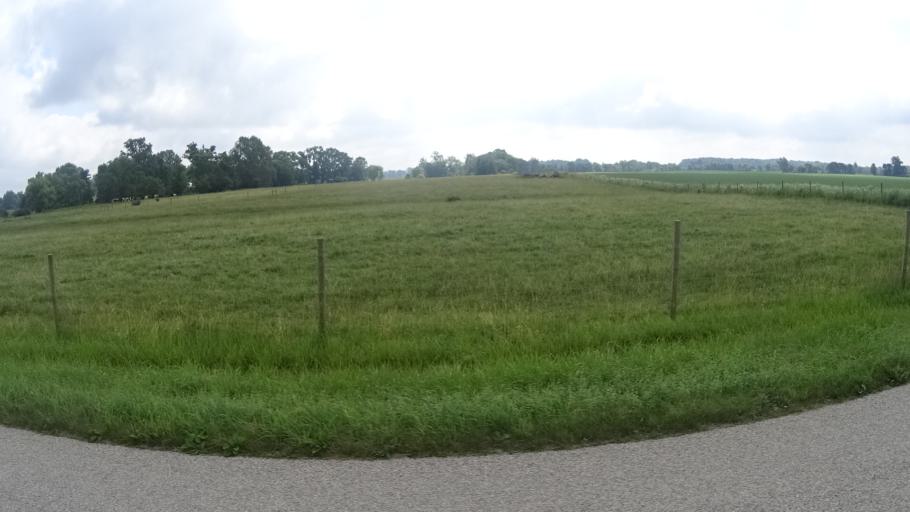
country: US
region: Ohio
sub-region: Huron County
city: Wakeman
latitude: 41.2995
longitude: -82.4658
